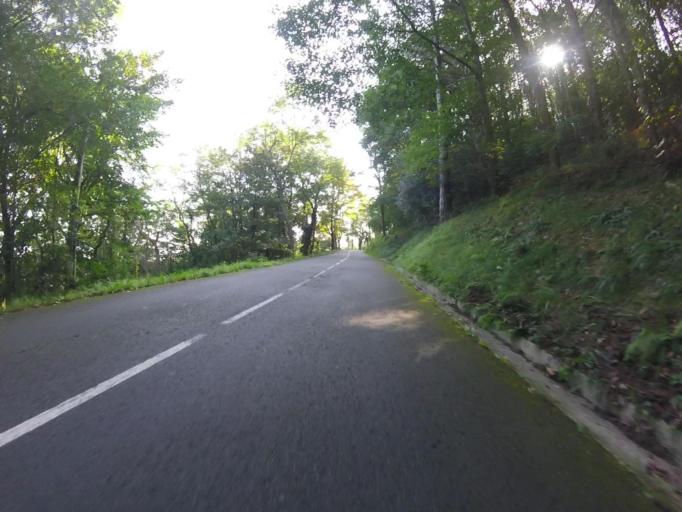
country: ES
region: Basque Country
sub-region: Provincia de Guipuzcoa
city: Irun
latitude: 43.3318
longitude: -1.7671
